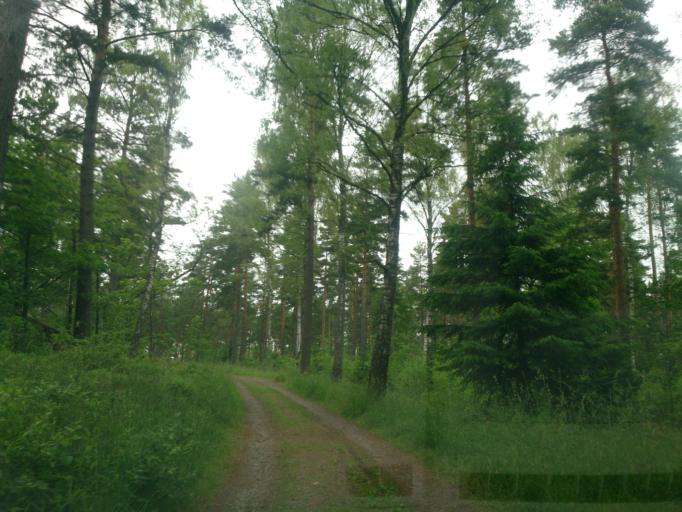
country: SE
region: OEstergoetland
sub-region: Atvidabergs Kommun
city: Atvidaberg
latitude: 58.2074
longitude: 16.0005
